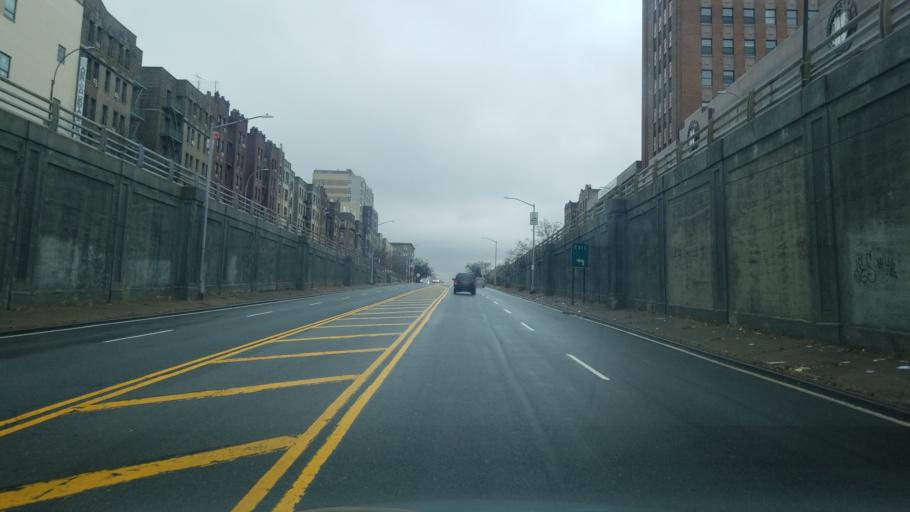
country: US
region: New York
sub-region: New York County
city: Inwood
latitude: 40.8628
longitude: -73.8969
